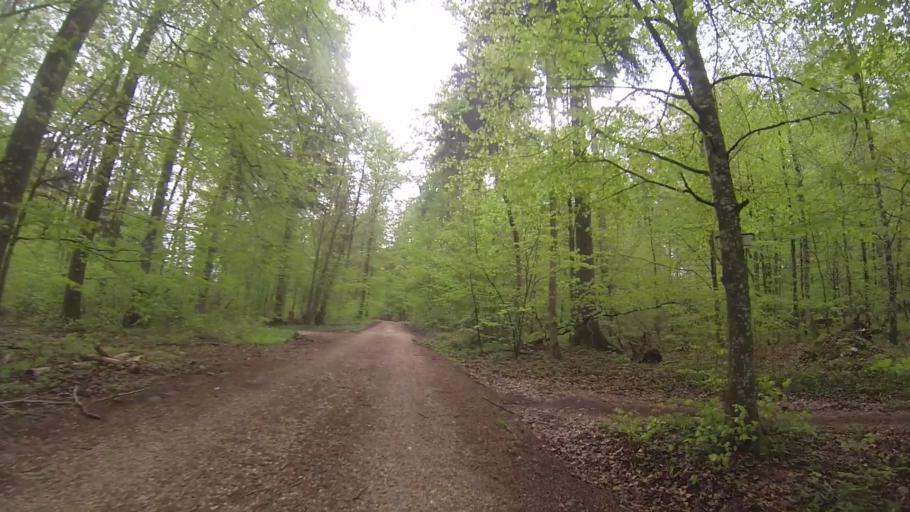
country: DE
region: Baden-Wuerttemberg
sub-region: Regierungsbezirk Stuttgart
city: Nattheim
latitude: 48.6690
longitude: 10.2198
